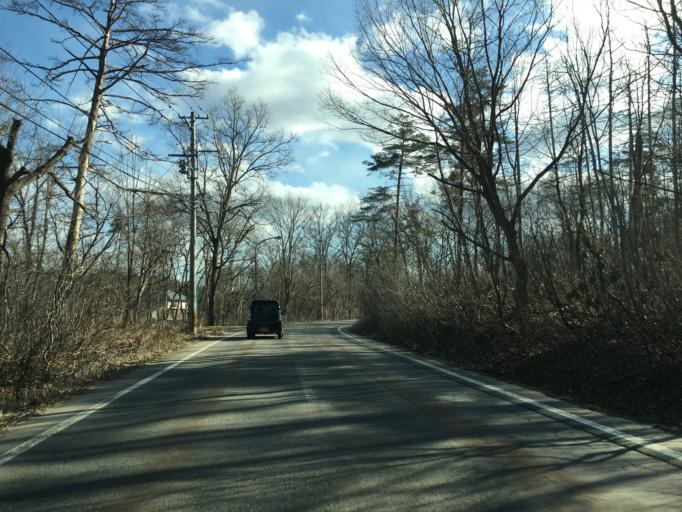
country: JP
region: Yamagata
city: Nagai
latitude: 37.9841
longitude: 140.0018
